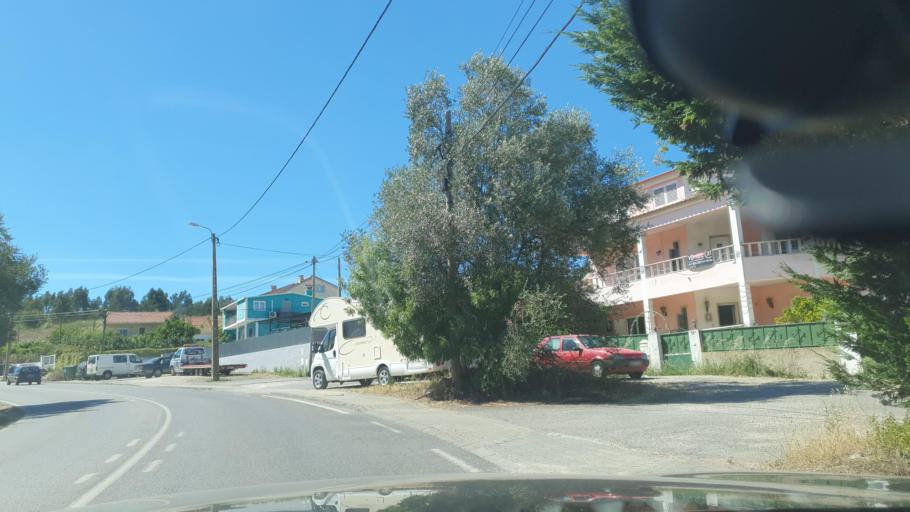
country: PT
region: Lisbon
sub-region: Sintra
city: Belas
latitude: 38.7825
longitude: -9.2541
